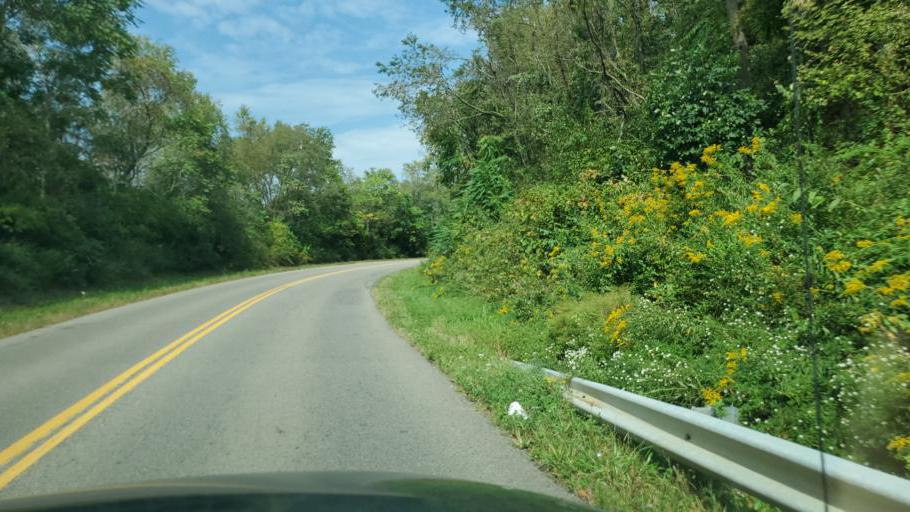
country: US
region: Ohio
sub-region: Muskingum County
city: Zanesville
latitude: 39.9479
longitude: -82.0674
